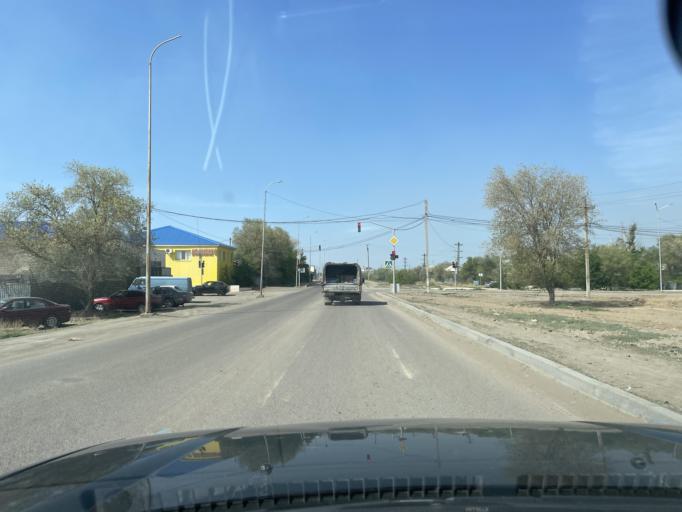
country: KZ
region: Qaraghandy
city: Zhezqazghan
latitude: 47.7869
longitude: 67.7116
